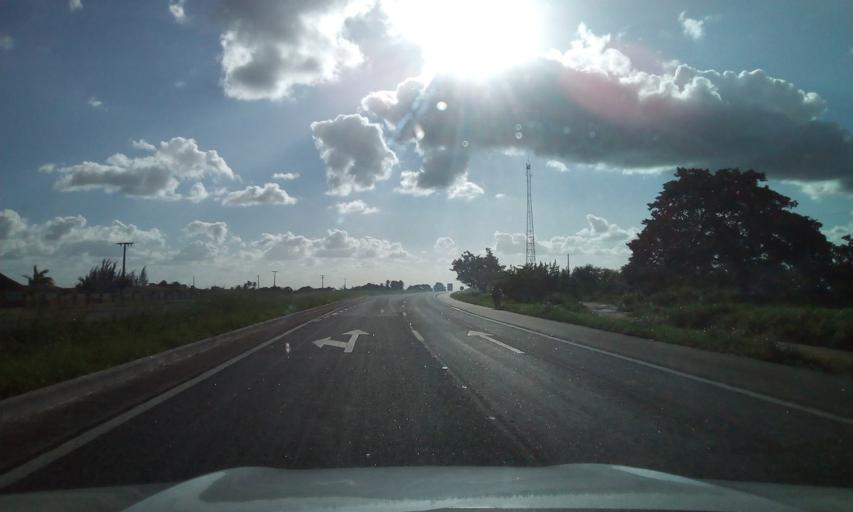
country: BR
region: Paraiba
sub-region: Cruz Do Espirito Santo
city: Cruz do Espirito Santo
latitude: -7.2052
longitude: -35.1497
